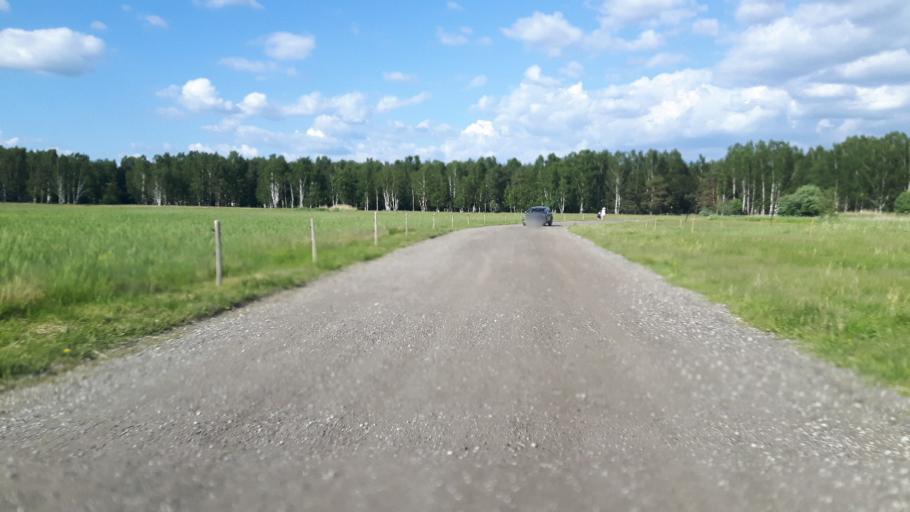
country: EE
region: Paernumaa
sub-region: Paernu linn
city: Parnu
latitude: 58.3467
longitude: 24.5633
